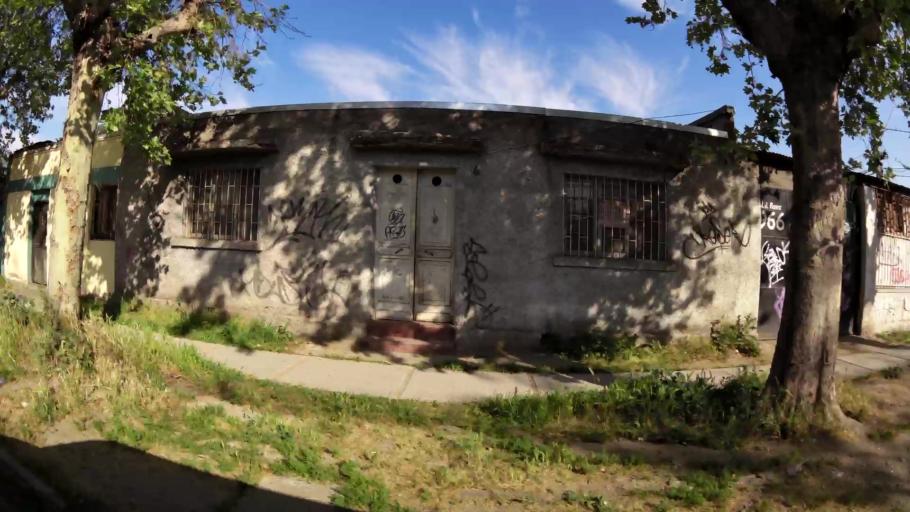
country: CL
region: Santiago Metropolitan
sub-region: Provincia de Maipo
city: San Bernardo
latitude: -33.6020
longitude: -70.7029
